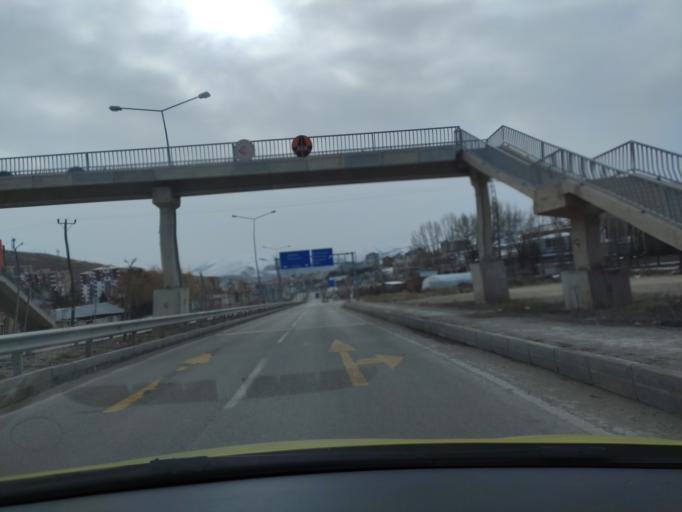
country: TR
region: Bayburt
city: Bayburt
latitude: 40.2622
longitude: 40.2083
